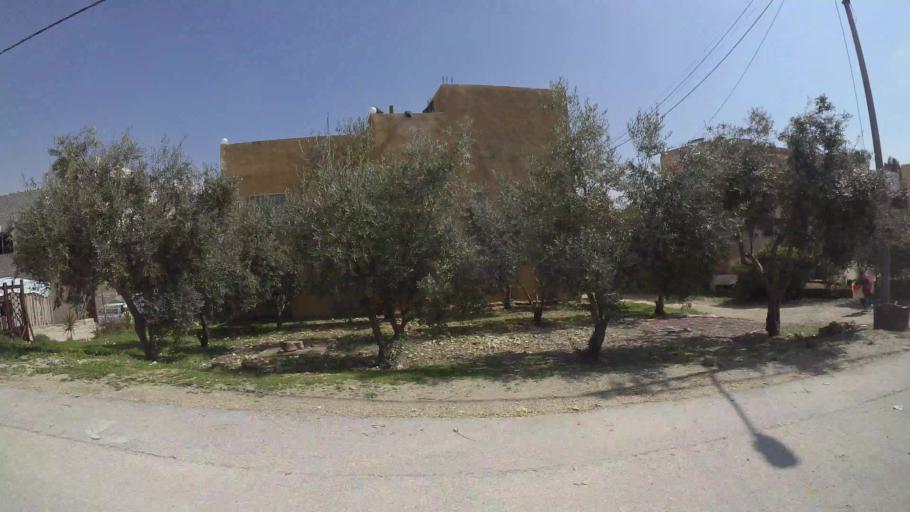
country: JO
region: Amman
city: Al Bunayyat ash Shamaliyah
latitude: 31.8865
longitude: 35.8969
